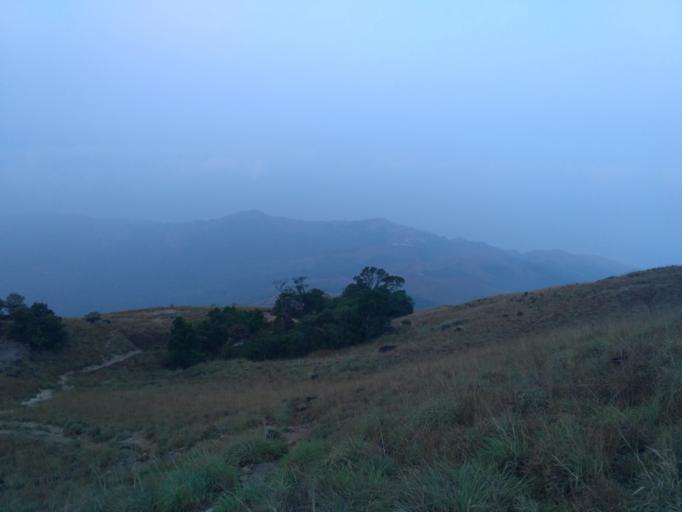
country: IN
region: Karnataka
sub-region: Kodagu
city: Somvarpet
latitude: 12.6636
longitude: 75.6689
